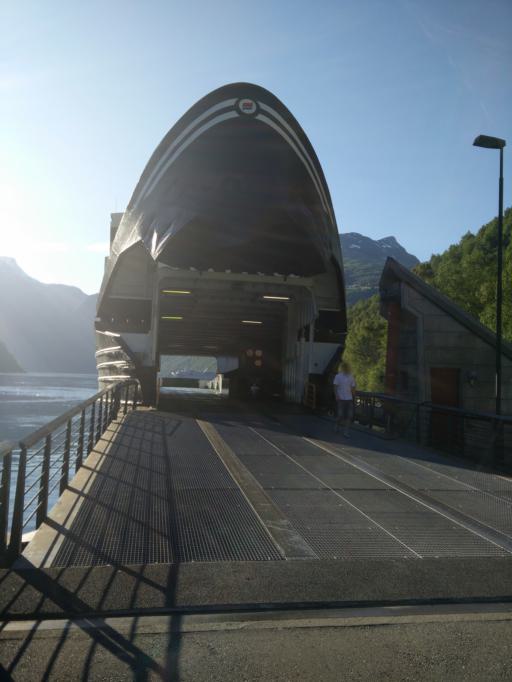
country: NO
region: More og Romsdal
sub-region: Norddal
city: Valldal
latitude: 62.1035
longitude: 7.2030
